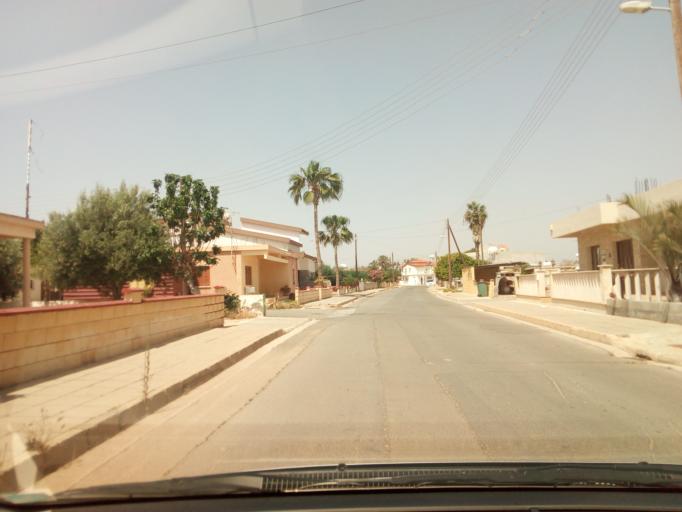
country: CY
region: Ammochostos
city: Liopetri
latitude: 34.9744
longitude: 33.8504
